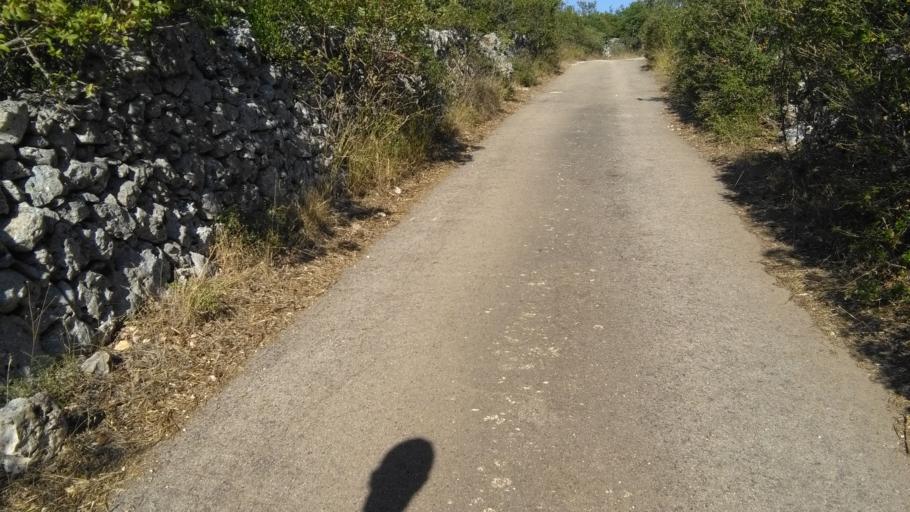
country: IT
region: Apulia
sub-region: Provincia di Bari
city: Putignano
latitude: 40.8204
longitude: 17.0369
